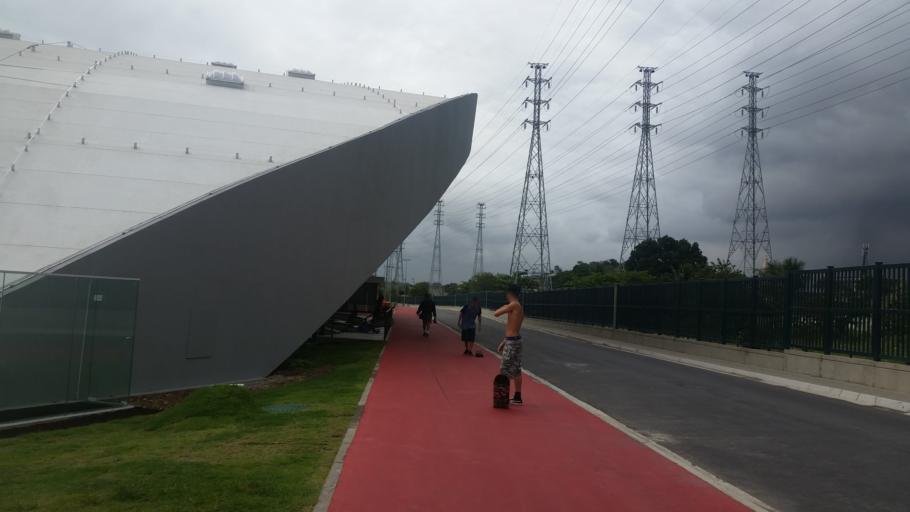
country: BR
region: Rio de Janeiro
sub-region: Sao Joao De Meriti
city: Sao Joao de Meriti
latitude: -22.8548
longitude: -43.3526
